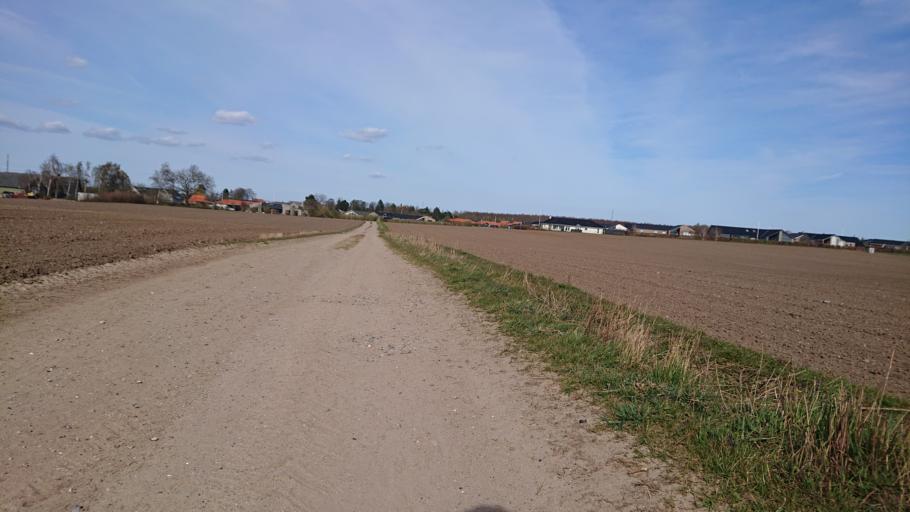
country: DK
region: South Denmark
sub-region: Nyborg Kommune
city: Nyborg
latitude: 55.3042
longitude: 10.7490
